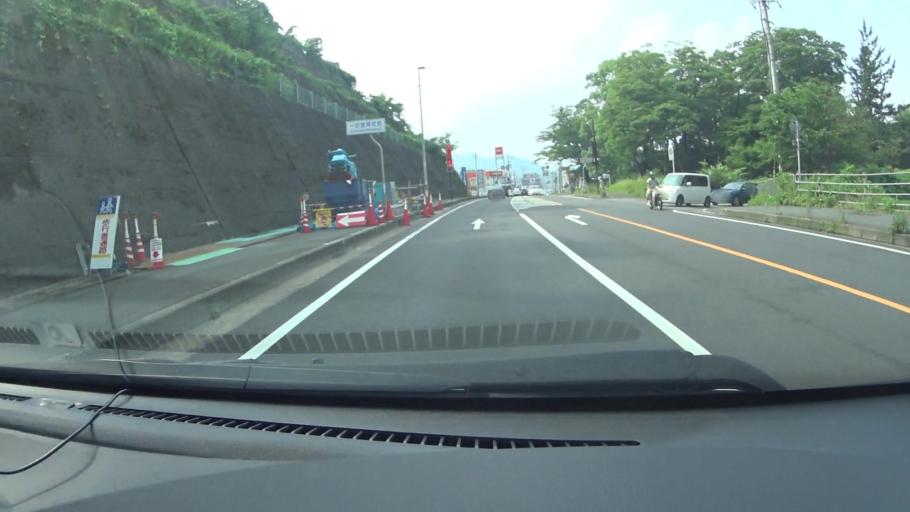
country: JP
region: Kyoto
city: Maizuru
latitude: 35.4185
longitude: 135.3309
